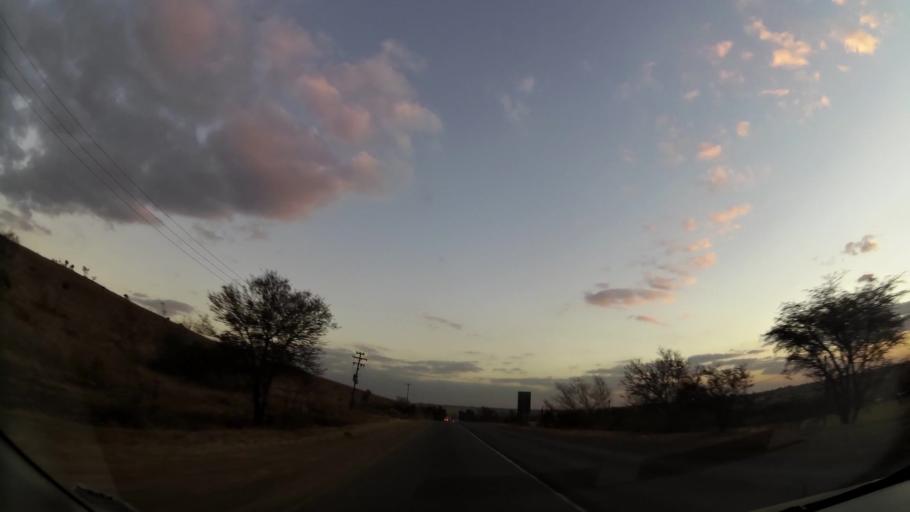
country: ZA
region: Gauteng
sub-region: West Rand District Municipality
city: Krugersdorp
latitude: -26.0366
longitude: 27.7236
